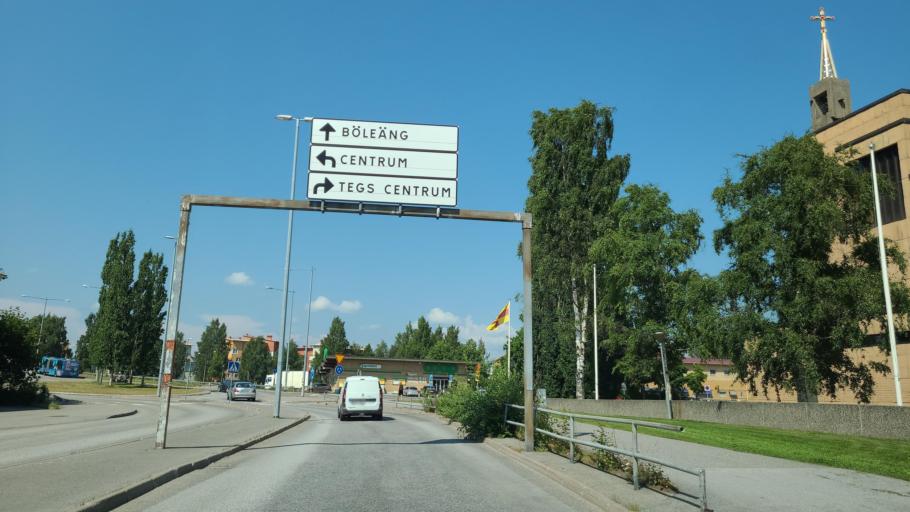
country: SE
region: Vaesterbotten
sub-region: Umea Kommun
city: Umea
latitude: 63.8192
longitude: 20.2544
